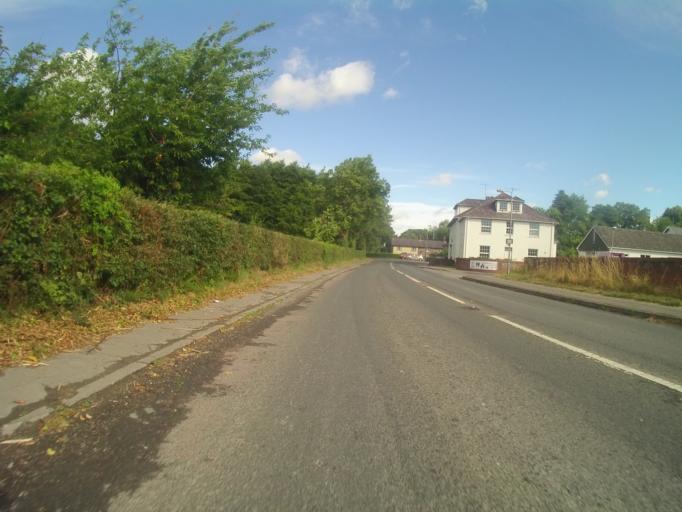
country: GB
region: England
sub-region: Wiltshire
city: Bulford
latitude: 51.1913
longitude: -1.7624
